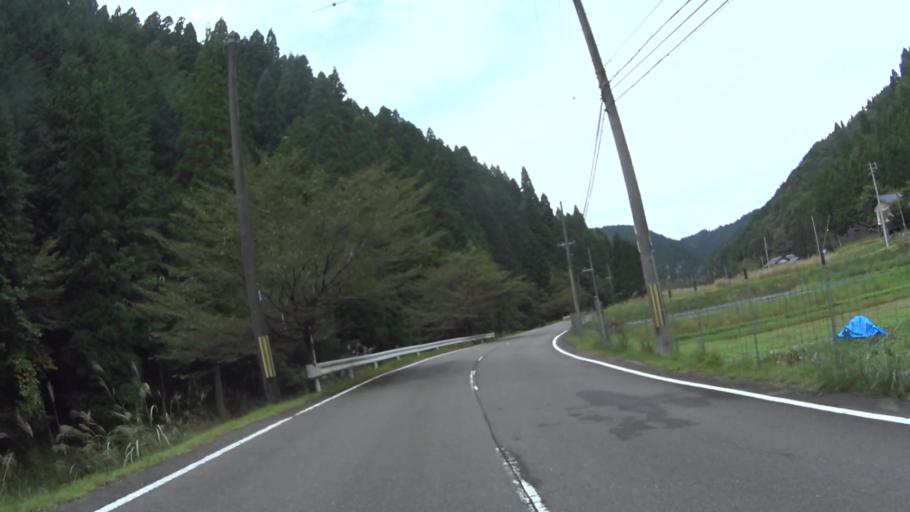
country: JP
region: Shiga Prefecture
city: Kitahama
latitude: 35.2619
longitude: 135.7511
